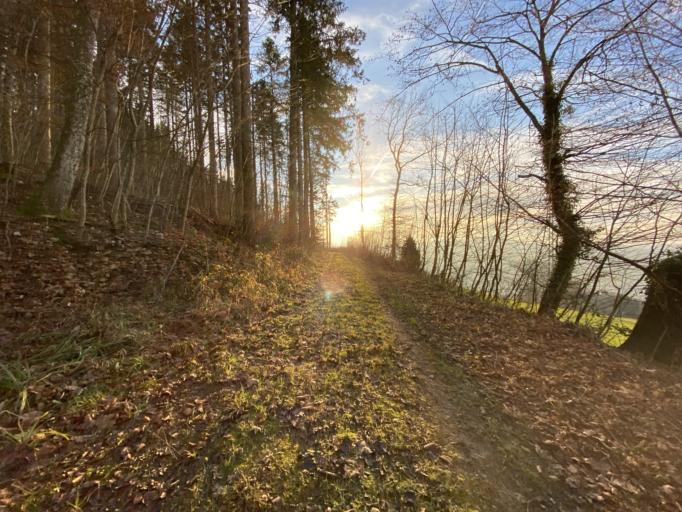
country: CH
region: Aargau
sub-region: Bezirk Laufenburg
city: Frick
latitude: 47.5136
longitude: 8.0390
